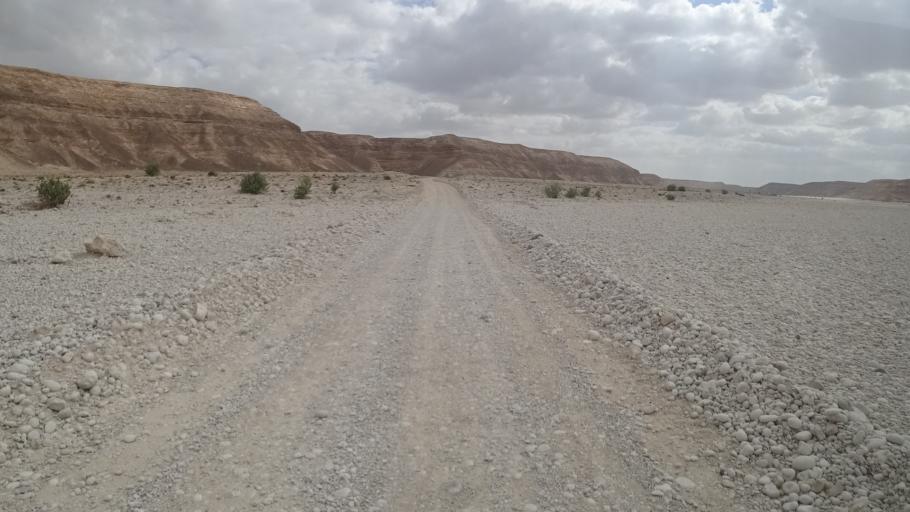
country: YE
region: Al Mahrah
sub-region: Shahan
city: Shihan as Sufla
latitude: 17.4641
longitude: 53.0070
